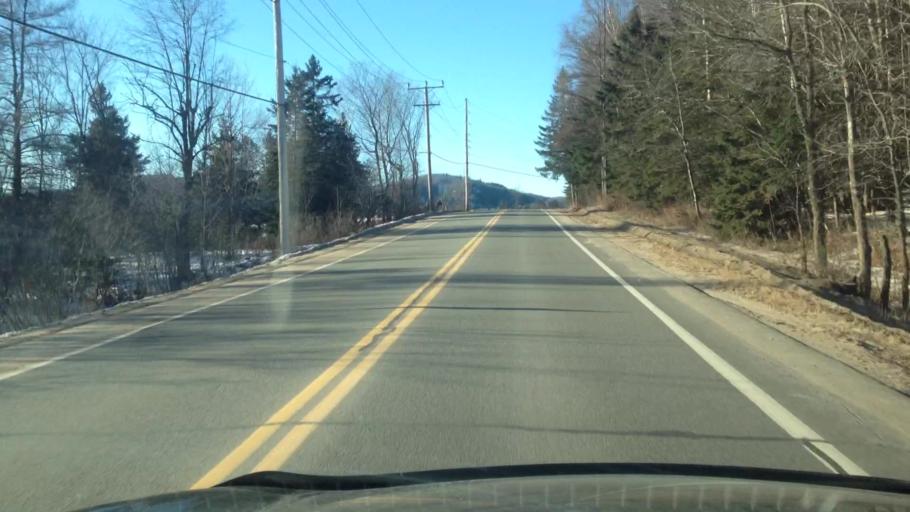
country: CA
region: Quebec
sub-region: Laurentides
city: Mont-Tremblant
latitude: 45.9891
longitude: -74.6131
